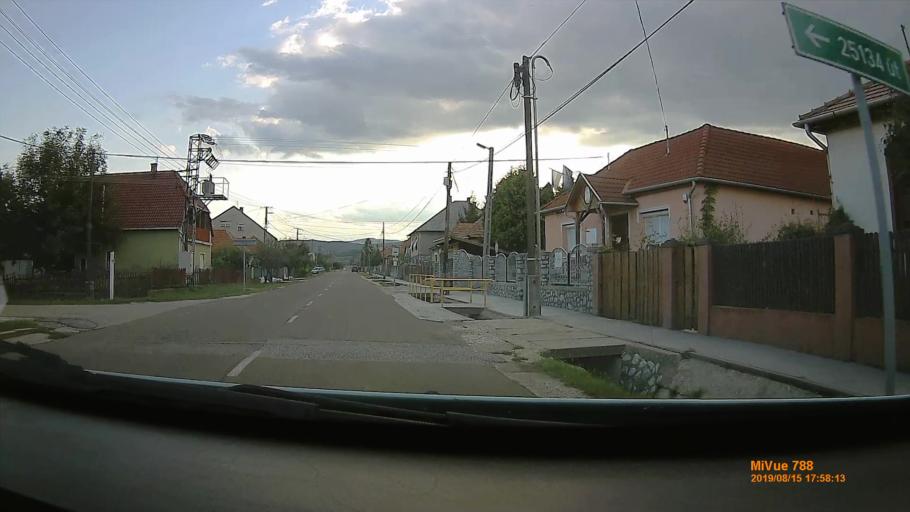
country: HU
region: Borsod-Abauj-Zemplen
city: Kazincbarcika
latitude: 48.1806
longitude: 20.6517
